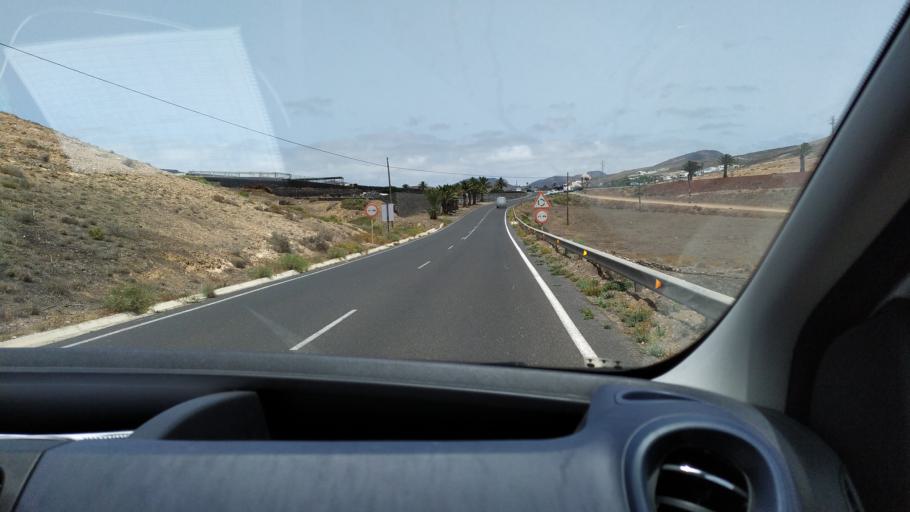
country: ES
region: Canary Islands
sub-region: Provincia de Las Palmas
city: Yaiza
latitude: 28.9391
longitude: -13.7425
